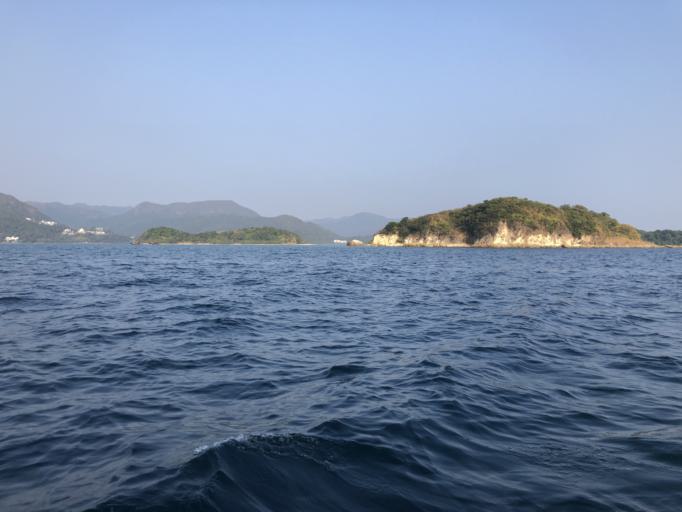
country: HK
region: Sai Kung
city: Sai Kung
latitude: 22.3737
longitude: 114.2820
